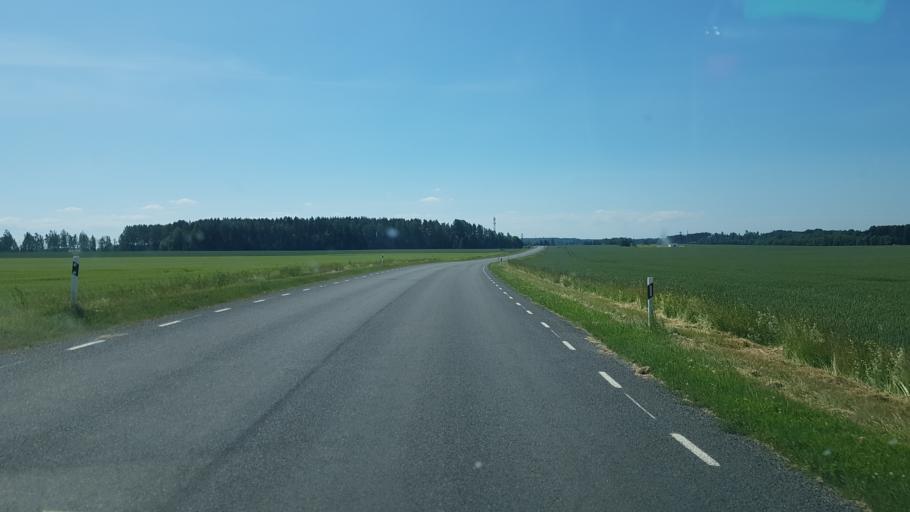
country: EE
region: Tartu
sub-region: UElenurme vald
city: Ulenurme
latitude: 58.3168
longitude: 26.8842
